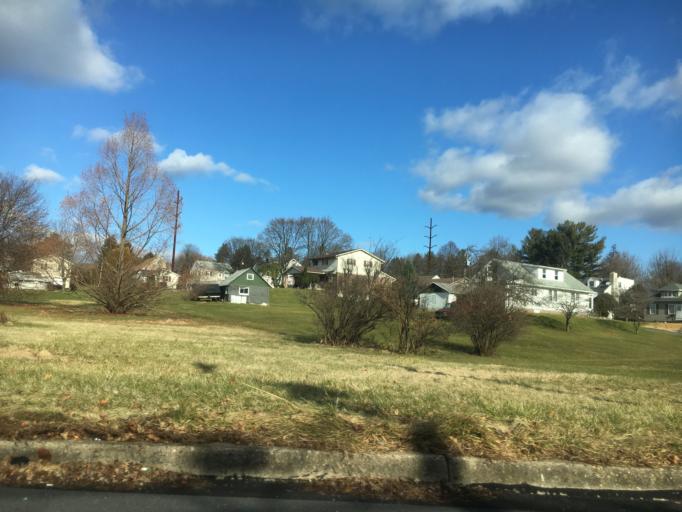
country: US
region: Pennsylvania
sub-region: Lehigh County
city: Egypt
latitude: 40.6801
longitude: -75.5367
